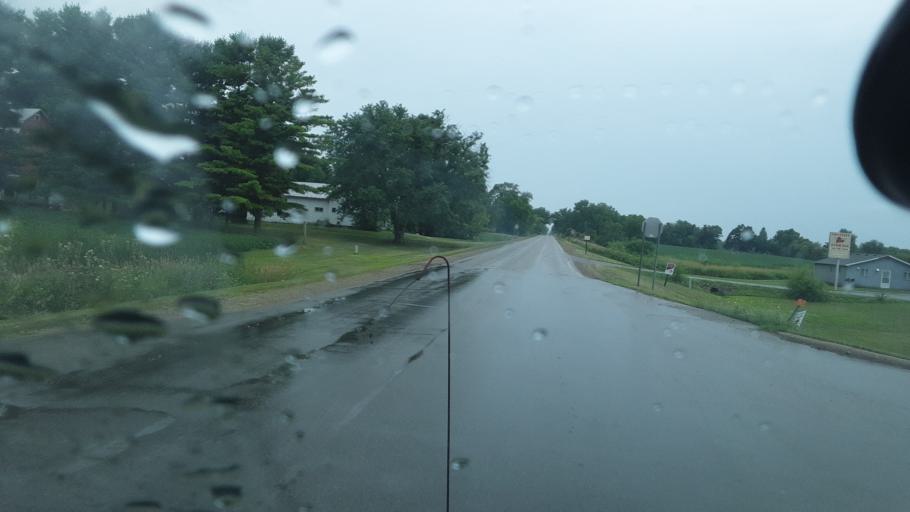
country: US
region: Michigan
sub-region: Hillsdale County
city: Reading
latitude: 41.7081
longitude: -84.7508
